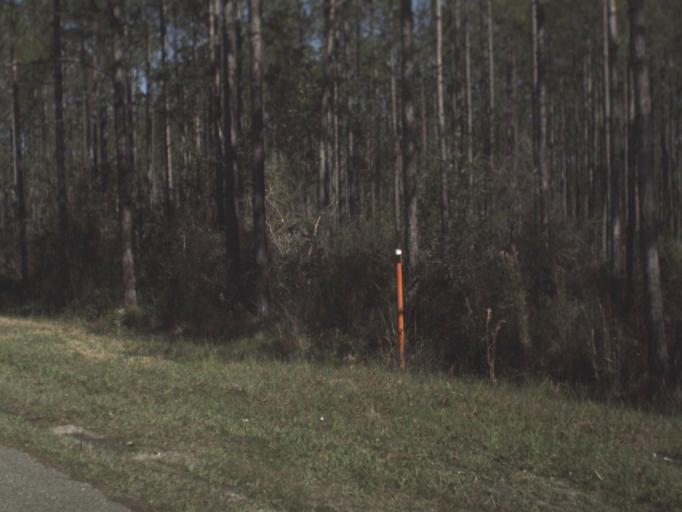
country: US
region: Florida
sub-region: Gulf County
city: Port Saint Joe
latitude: 29.8591
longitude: -85.2467
